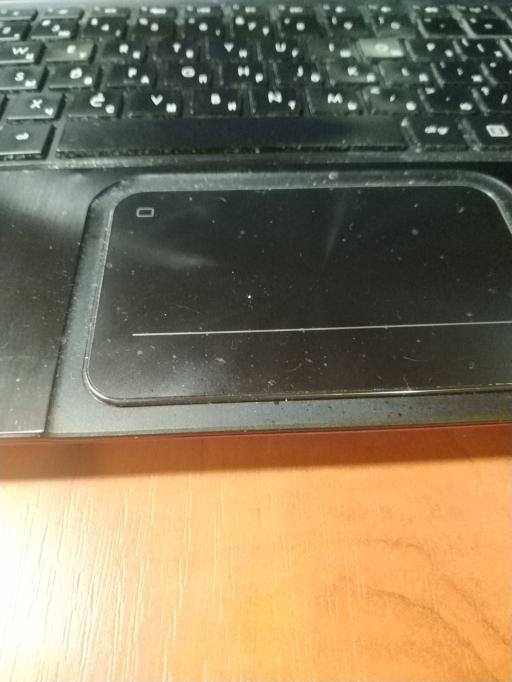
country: RU
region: Tverskaya
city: Likhoslavl'
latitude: 57.1282
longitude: 35.4641
